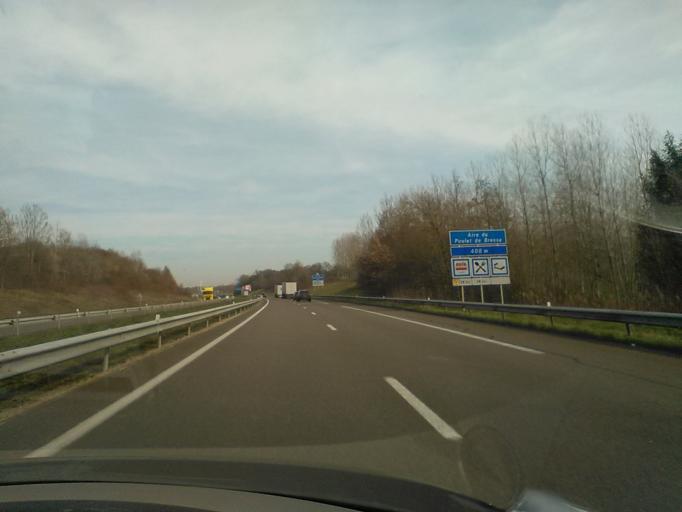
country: FR
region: Franche-Comte
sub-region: Departement du Jura
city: Saint-Amour
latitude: 46.4881
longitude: 5.3110
